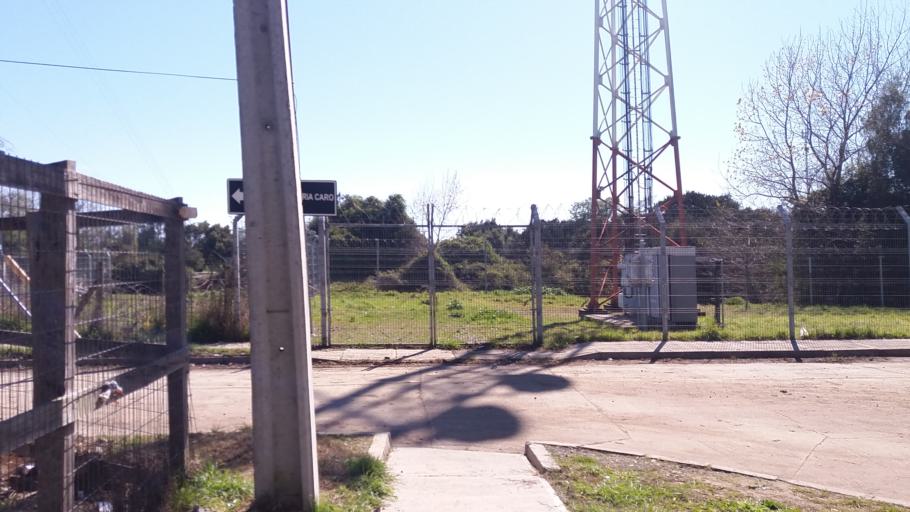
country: CL
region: Araucania
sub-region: Provincia de Cautin
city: Carahue
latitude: -39.1767
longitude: -73.1690
